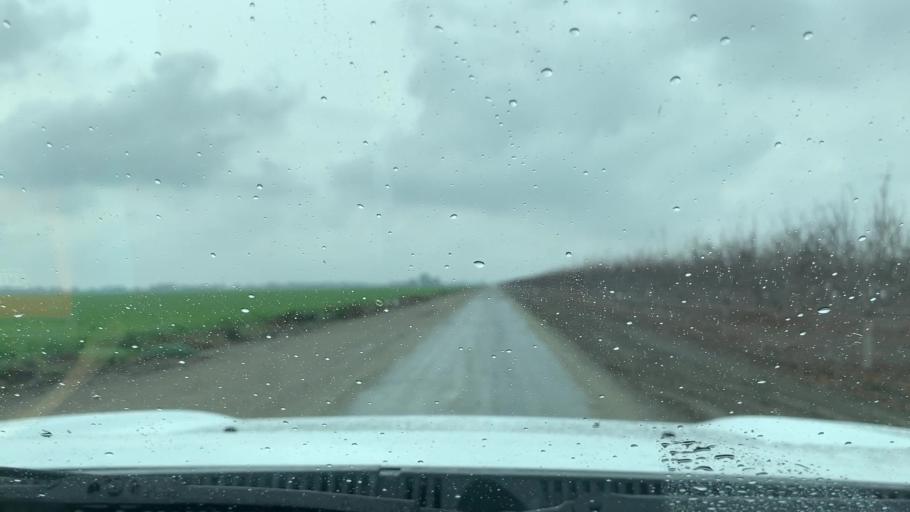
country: US
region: California
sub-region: Kings County
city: Corcoran
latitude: 36.0243
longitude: -119.5004
